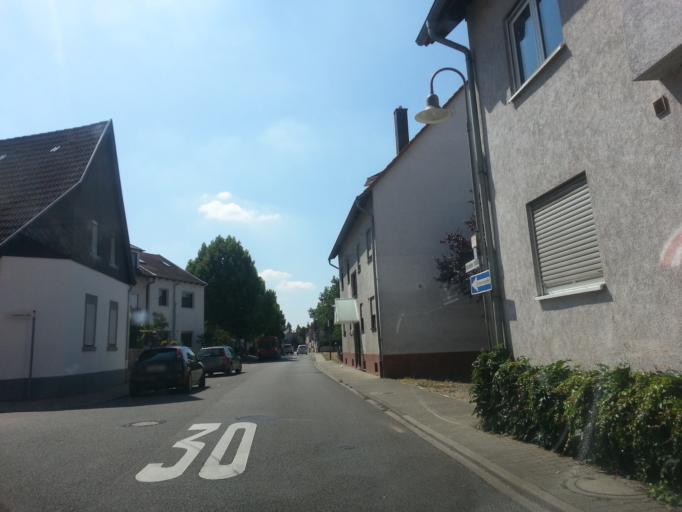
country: DE
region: Baden-Wuerttemberg
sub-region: Karlsruhe Region
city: Bruhl
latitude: 49.3978
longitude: 8.5325
